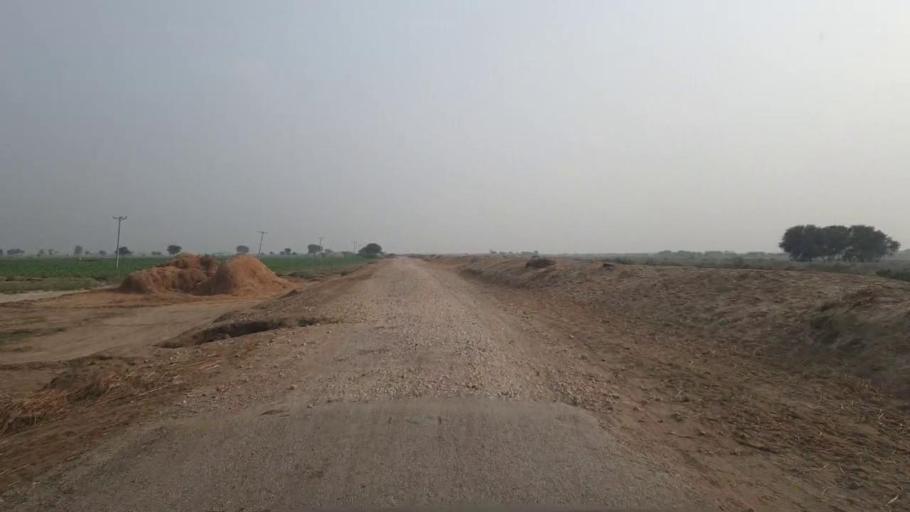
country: PK
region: Sindh
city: Mirpur Batoro
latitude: 24.5737
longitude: 68.3976
